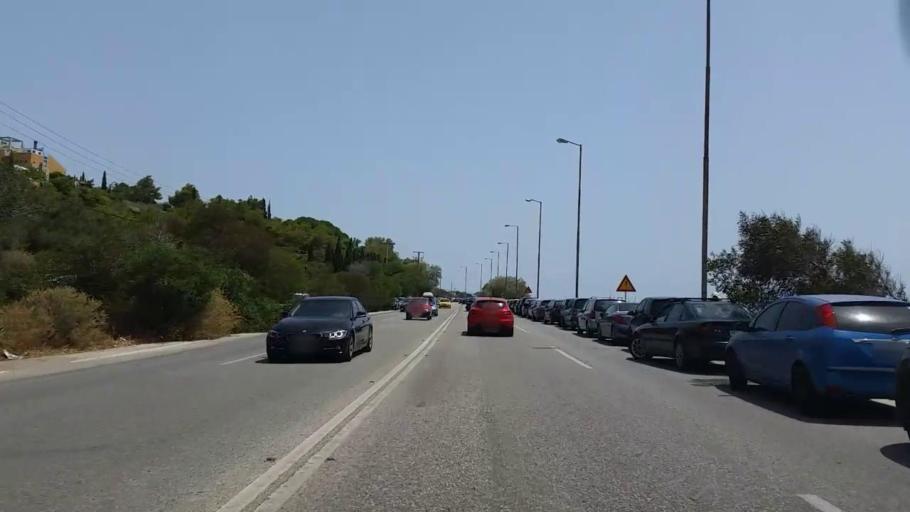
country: GR
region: Attica
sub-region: Nomarchia Anatolikis Attikis
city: Saronida
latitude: 37.7232
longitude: 23.9086
